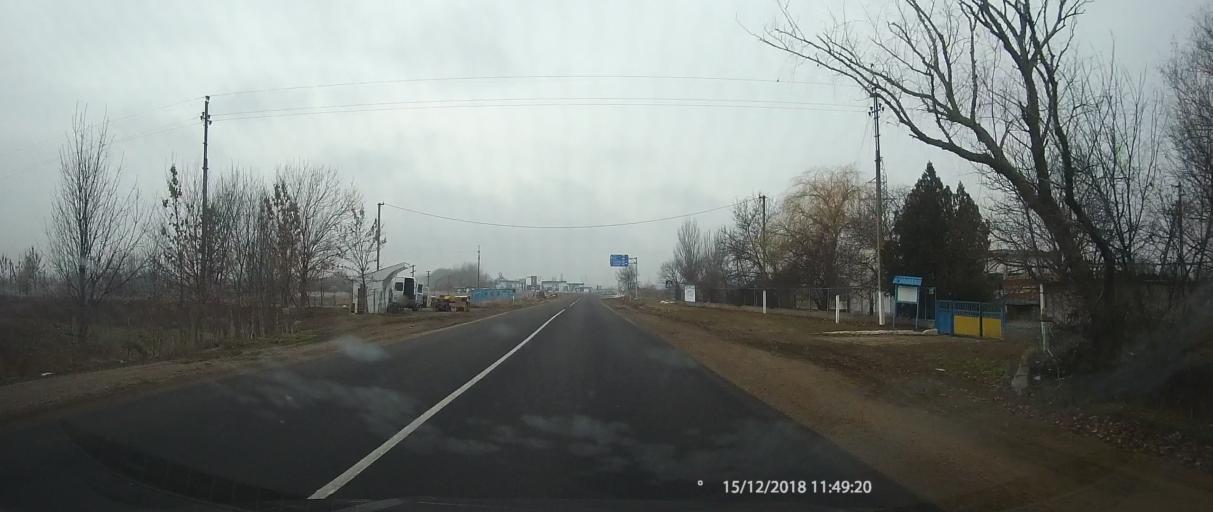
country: UA
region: Odessa
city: Bilyayivka
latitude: 46.4109
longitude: 30.1296
